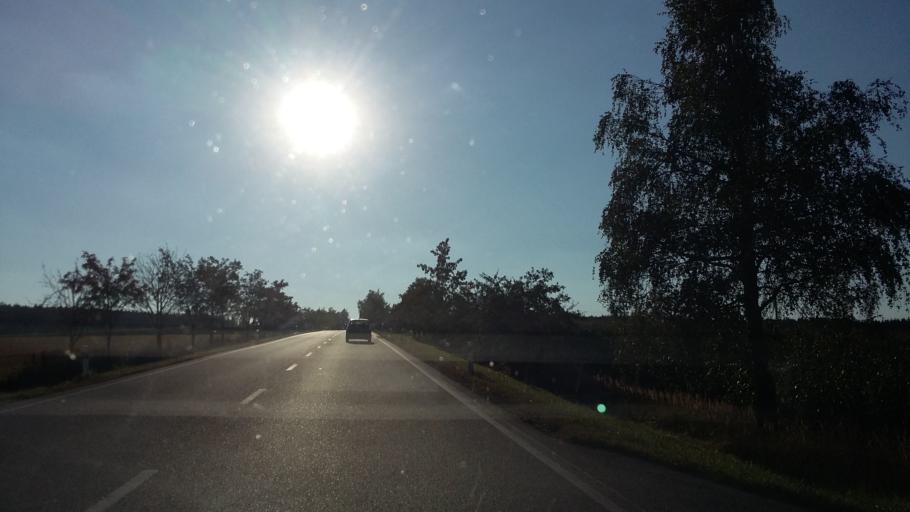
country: CZ
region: Vysocina
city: Merin
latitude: 49.4007
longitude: 15.8313
